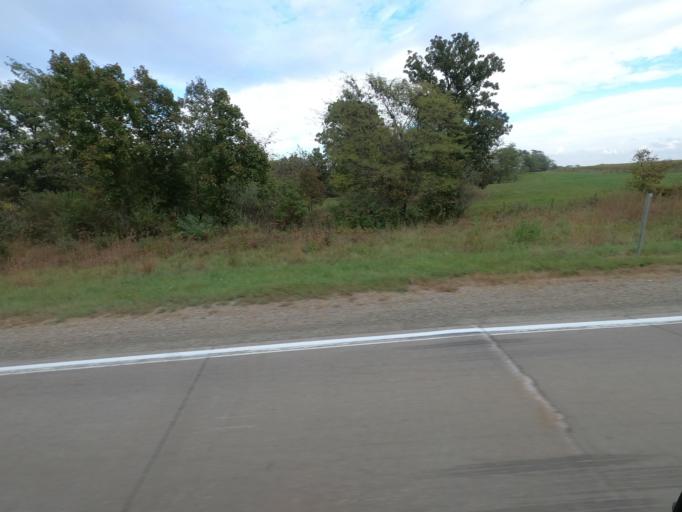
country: US
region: Iowa
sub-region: Henry County
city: Mount Pleasant
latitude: 40.7880
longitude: -91.7030
